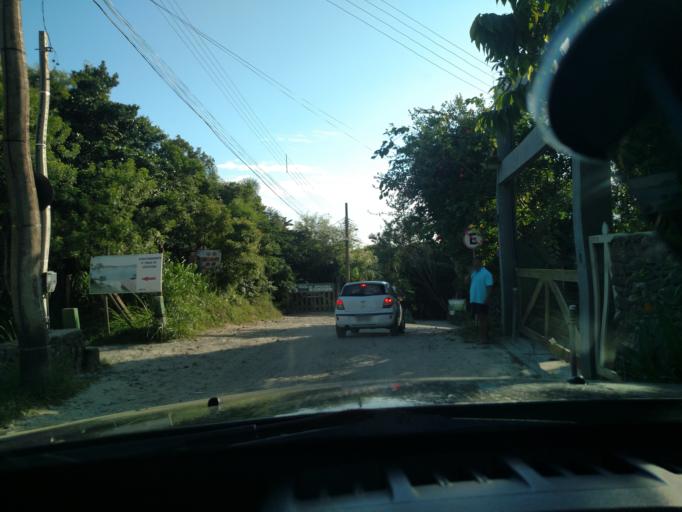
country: BR
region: Santa Catarina
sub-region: Porto Belo
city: Porto Belo
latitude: -27.1440
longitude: -48.4783
